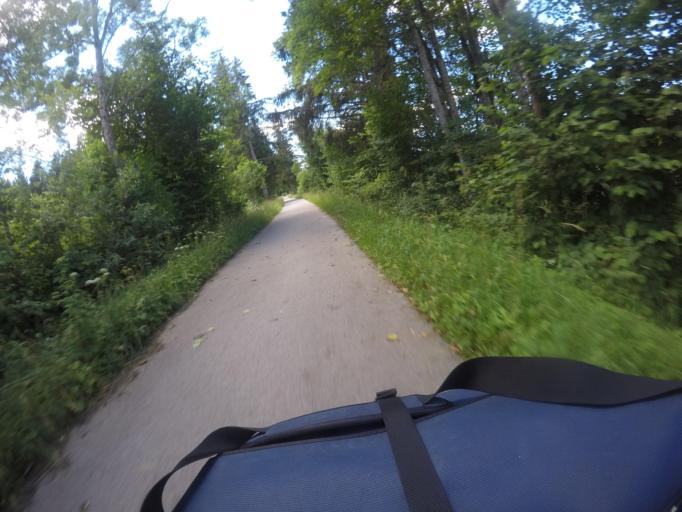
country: DE
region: Bavaria
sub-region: Swabia
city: Lechbruck
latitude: 47.6882
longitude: 10.7673
